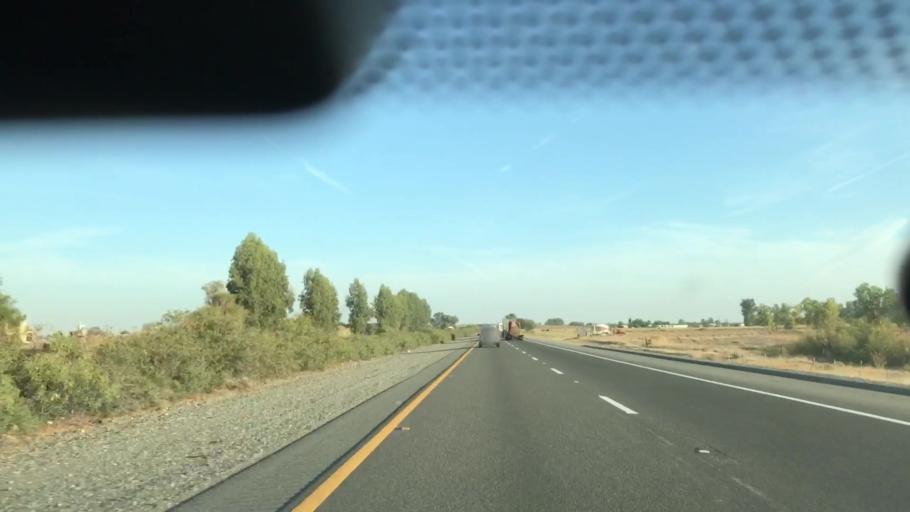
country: US
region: California
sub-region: Glenn County
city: Orland
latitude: 39.7747
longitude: -122.2047
